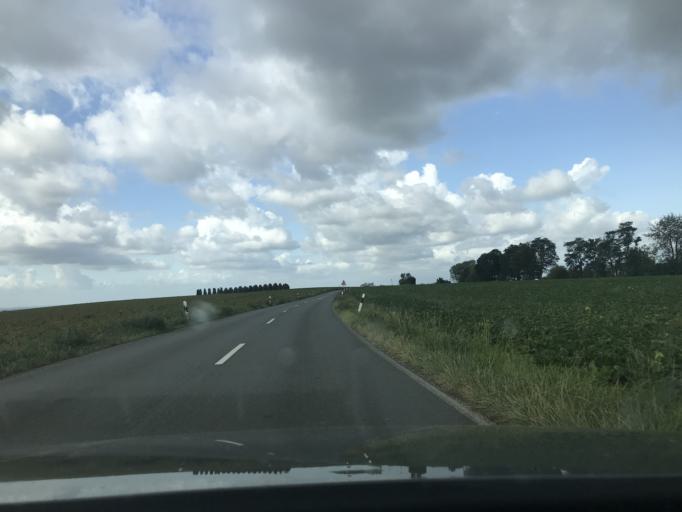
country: DE
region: North Rhine-Westphalia
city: Haan
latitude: 51.2114
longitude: 6.9949
